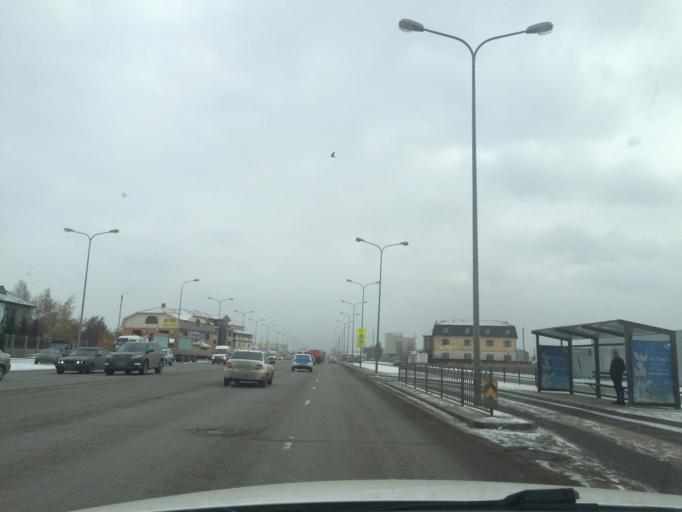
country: KZ
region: Astana Qalasy
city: Astana
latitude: 51.1785
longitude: 71.4692
